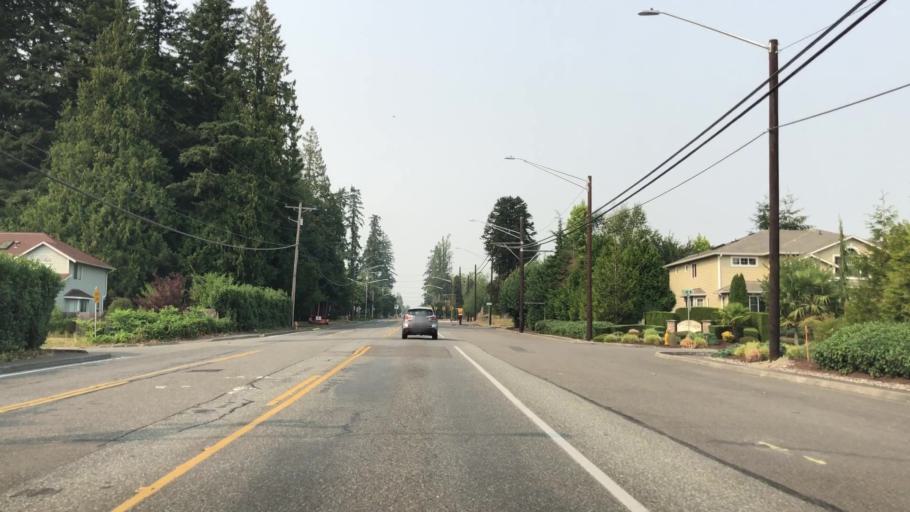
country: US
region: Washington
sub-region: Snohomish County
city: Alderwood Manor
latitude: 47.8443
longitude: -122.2818
